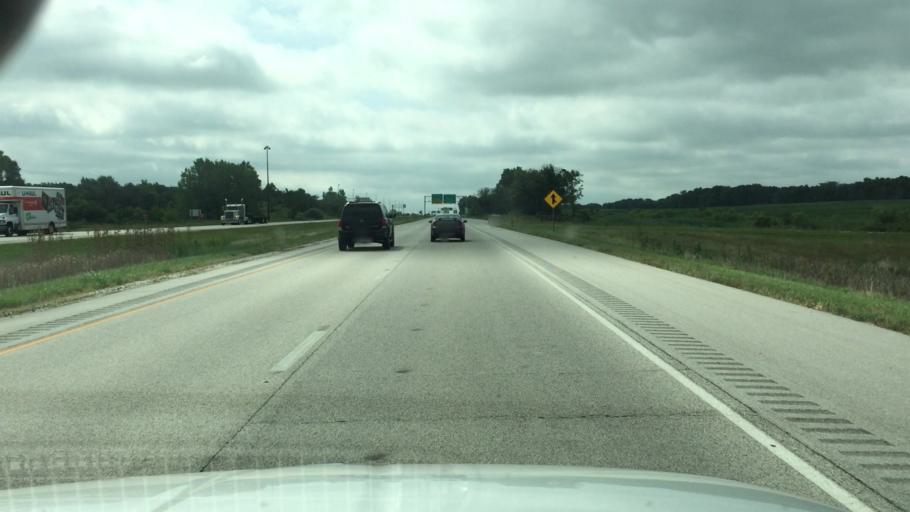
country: US
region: Illinois
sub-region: Henry County
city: Green Rock
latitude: 41.4539
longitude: -90.3364
